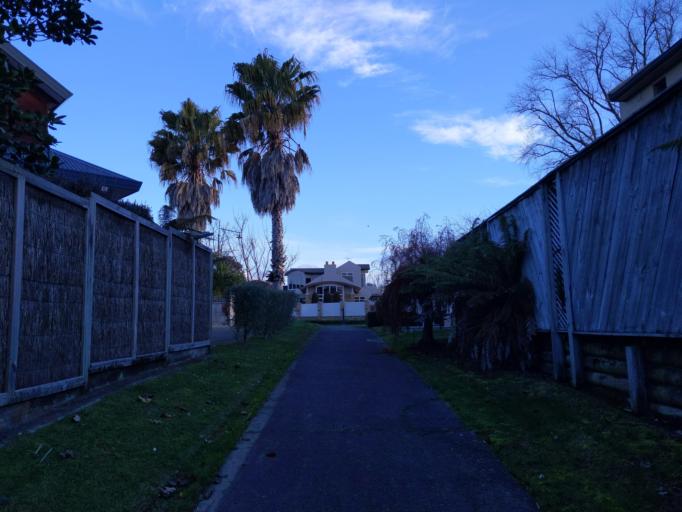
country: NZ
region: Waikato
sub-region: Hamilton City
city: Hamilton
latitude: -37.7417
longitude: 175.2766
